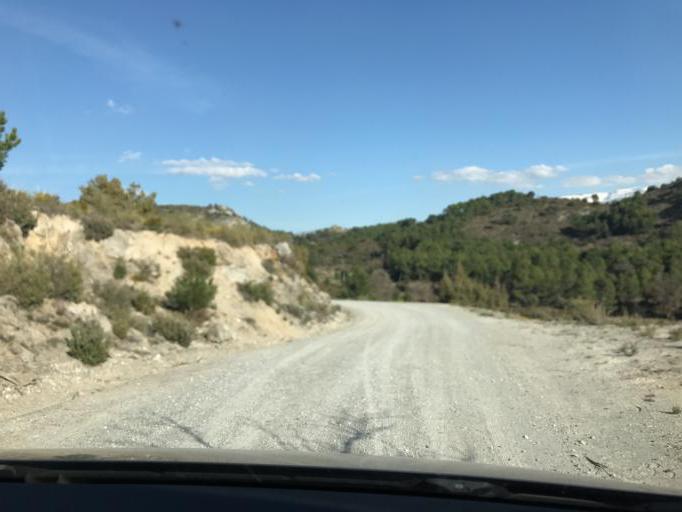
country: ES
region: Andalusia
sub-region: Provincia de Granada
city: Beas de Granada
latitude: 37.2413
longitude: -3.4473
